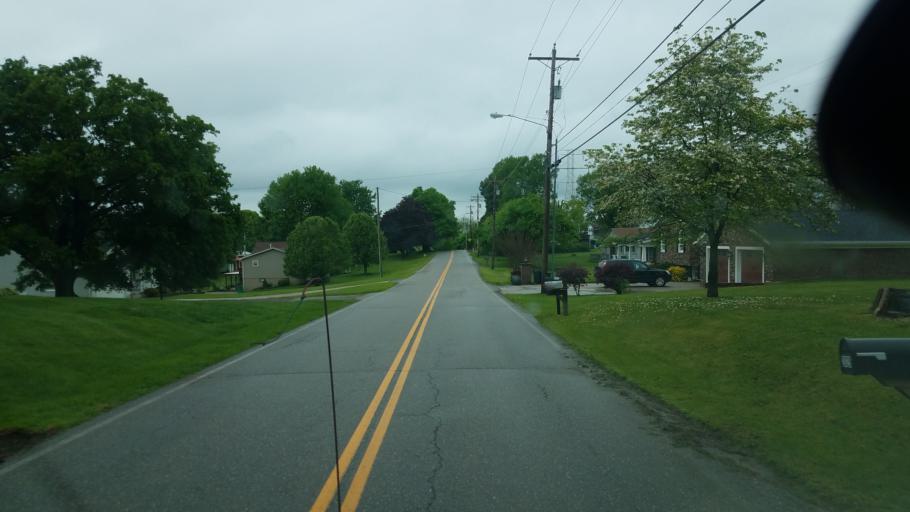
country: US
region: Ohio
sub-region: Jefferson County
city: Tiltonsville
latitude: 40.2565
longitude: -80.7533
